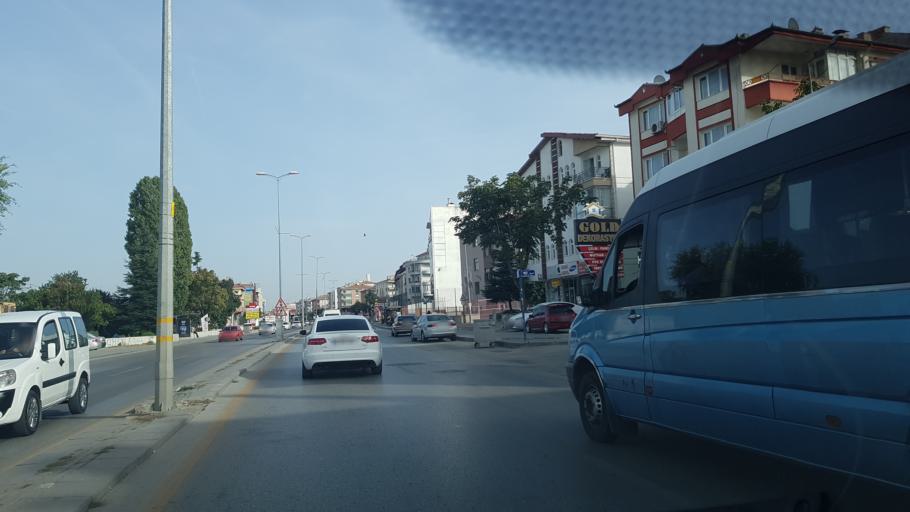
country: TR
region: Ankara
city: Etimesgut
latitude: 39.9516
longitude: 32.6474
